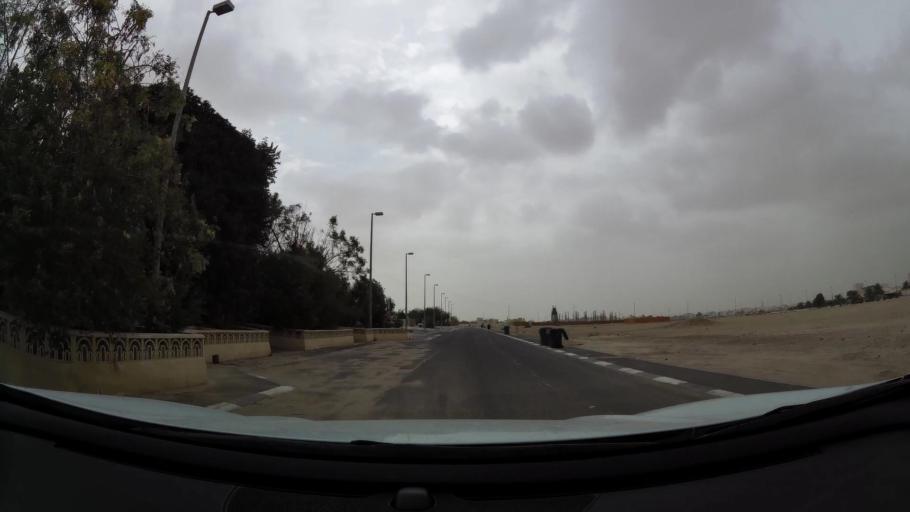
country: AE
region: Abu Dhabi
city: Abu Dhabi
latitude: 24.3671
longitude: 54.6663
